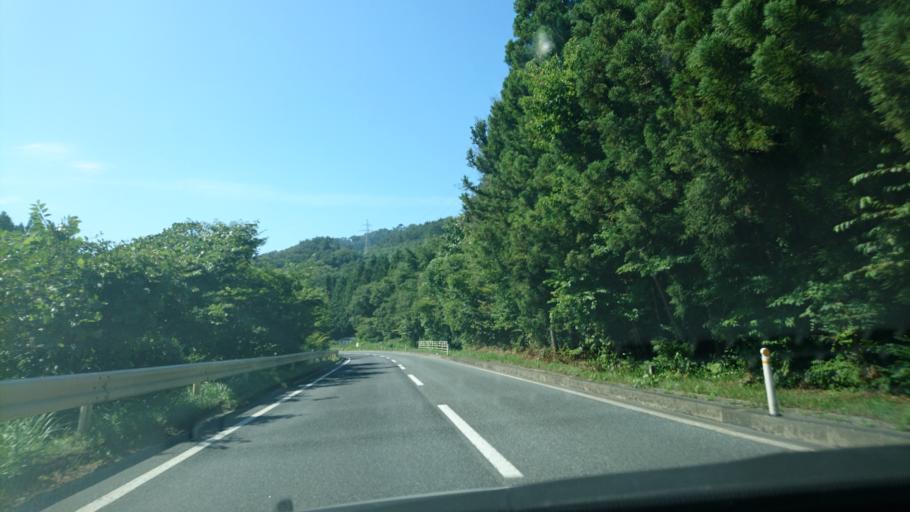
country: JP
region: Iwate
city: Ichinoseki
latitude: 38.9993
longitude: 141.2630
